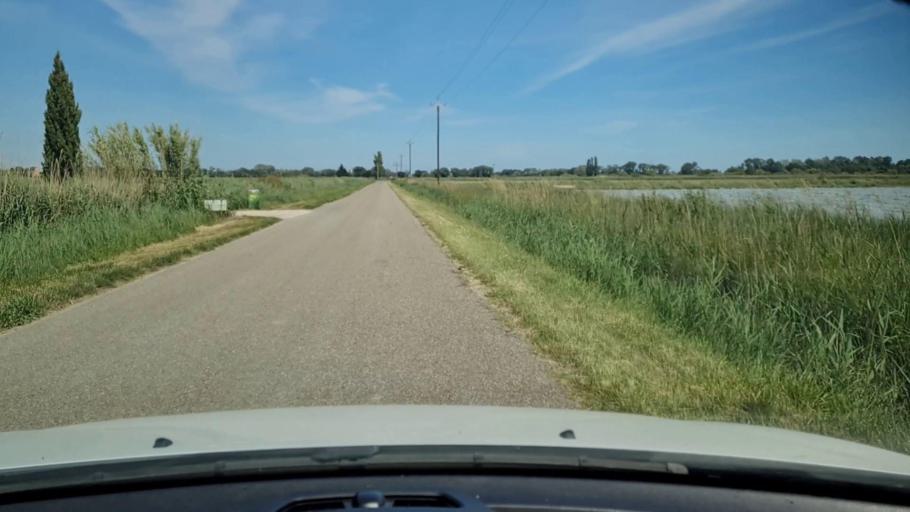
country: FR
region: Languedoc-Roussillon
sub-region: Departement du Gard
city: Saint-Gilles
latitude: 43.6033
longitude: 4.4556
